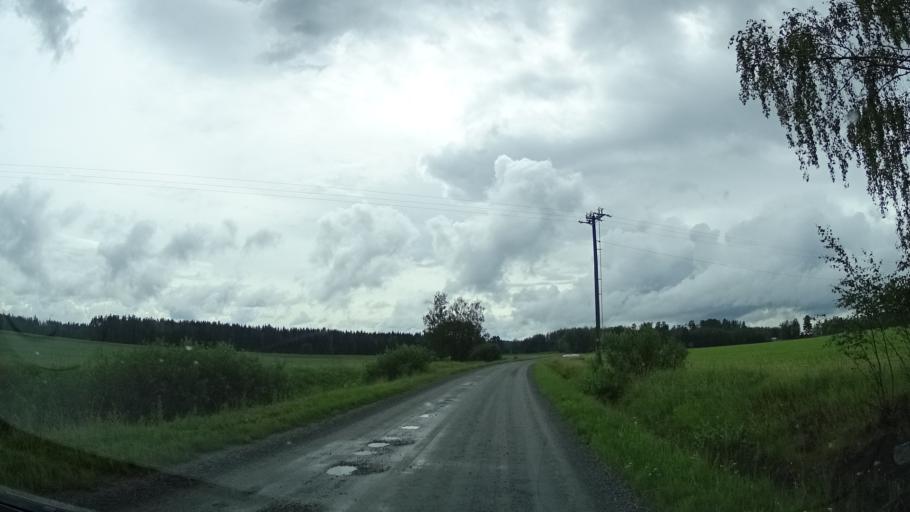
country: FI
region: Pirkanmaa
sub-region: Lounais-Pirkanmaa
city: Punkalaidun
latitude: 61.1181
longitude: 23.2912
